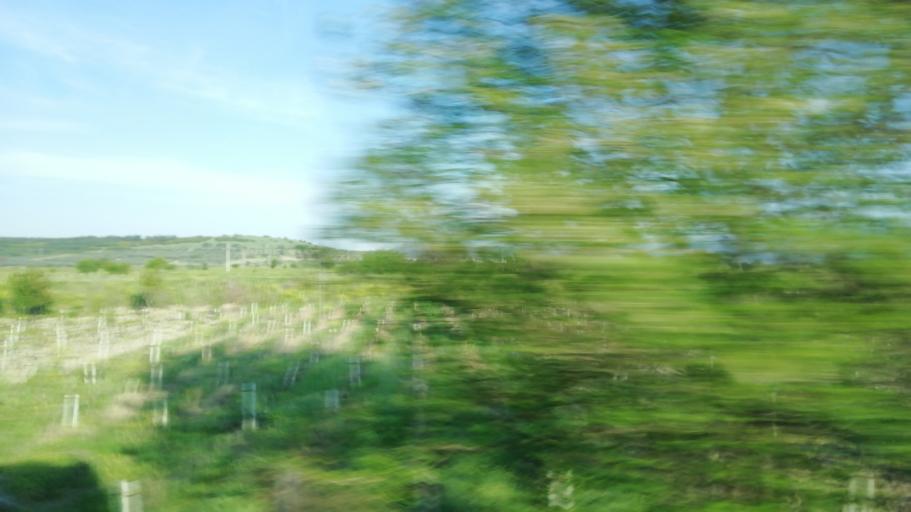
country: TR
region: Manisa
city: Halitpasa
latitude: 38.7767
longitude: 27.6636
